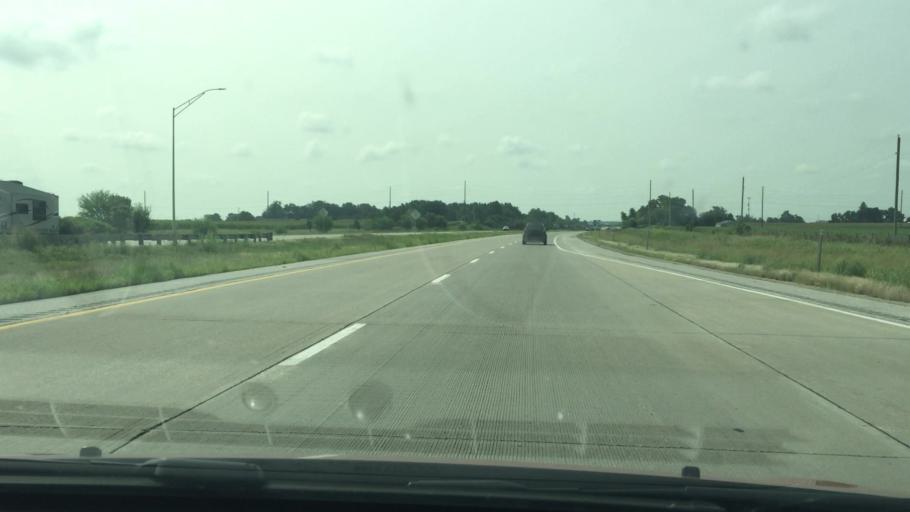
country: US
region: Iowa
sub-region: Scott County
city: Walcott
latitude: 41.5861
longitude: -90.6761
